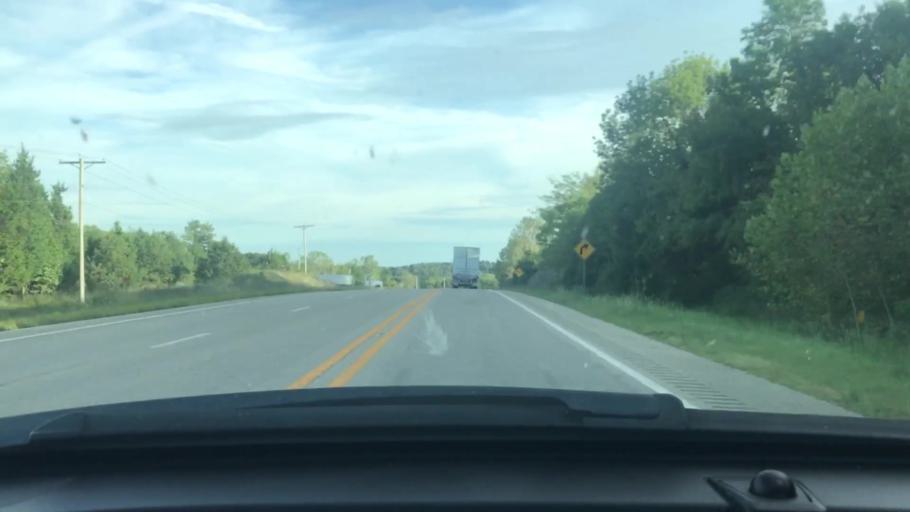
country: US
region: Arkansas
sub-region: Lawrence County
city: Hoxie
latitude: 36.1455
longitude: -91.1590
